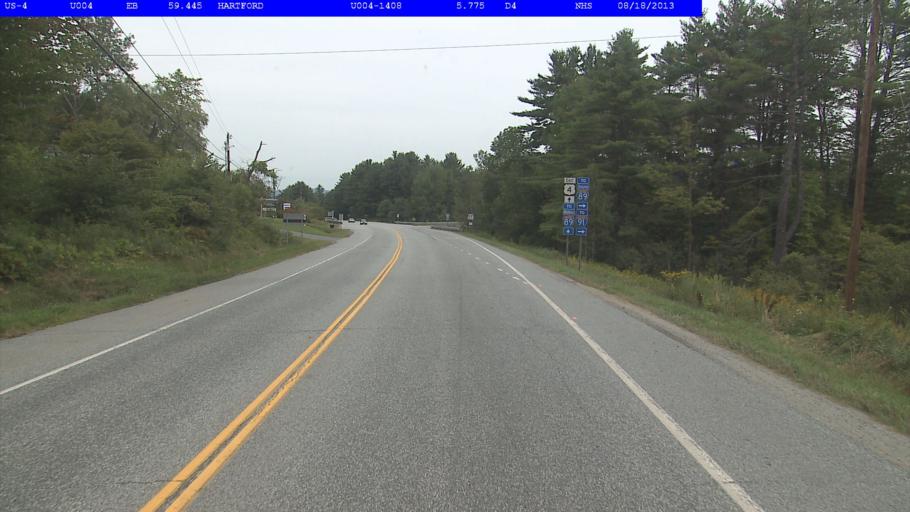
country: US
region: Vermont
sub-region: Windsor County
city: White River Junction
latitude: 43.6609
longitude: -72.3874
